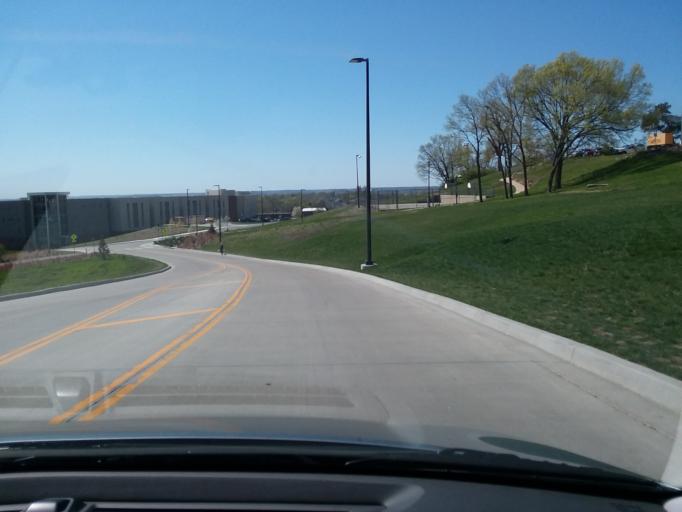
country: US
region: Kansas
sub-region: Douglas County
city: Lawrence
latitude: 38.9534
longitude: -95.2580
